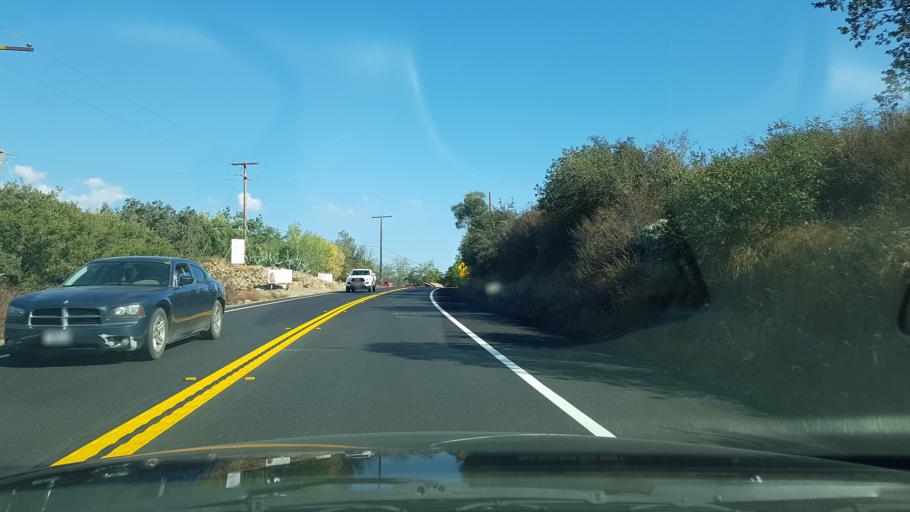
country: US
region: California
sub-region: San Diego County
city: San Diego Country Estates
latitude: 33.0675
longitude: -116.7281
